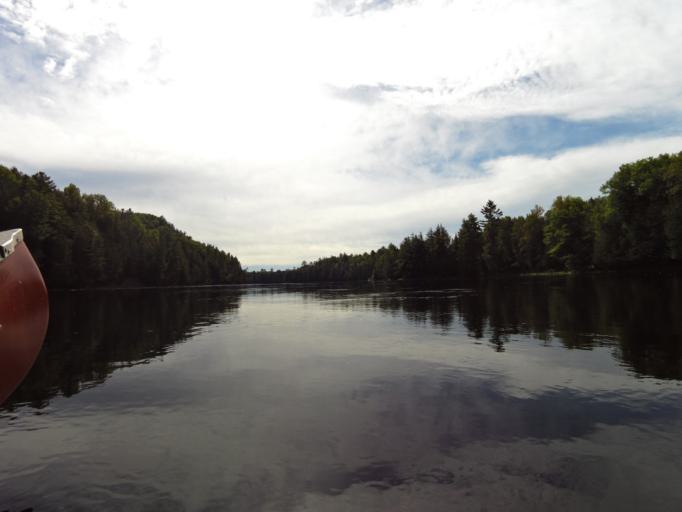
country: CA
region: Quebec
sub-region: Outaouais
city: Wakefield
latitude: 45.7823
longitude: -75.9455
